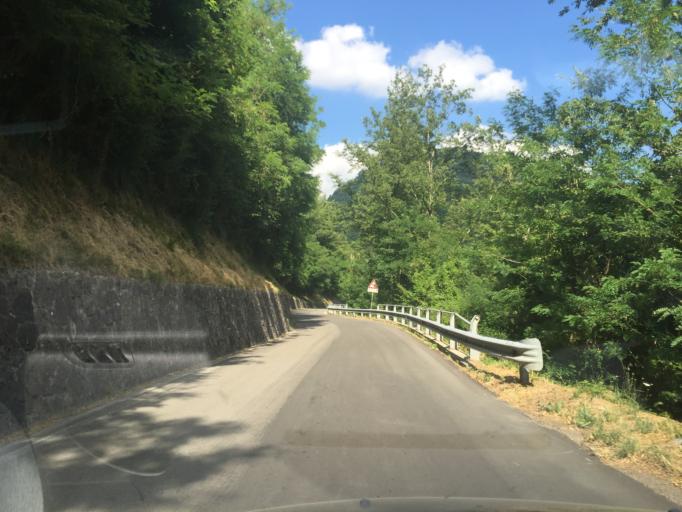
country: IT
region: Tuscany
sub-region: Provincia di Lucca
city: Fontana delle Monache
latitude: 44.1256
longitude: 10.3007
